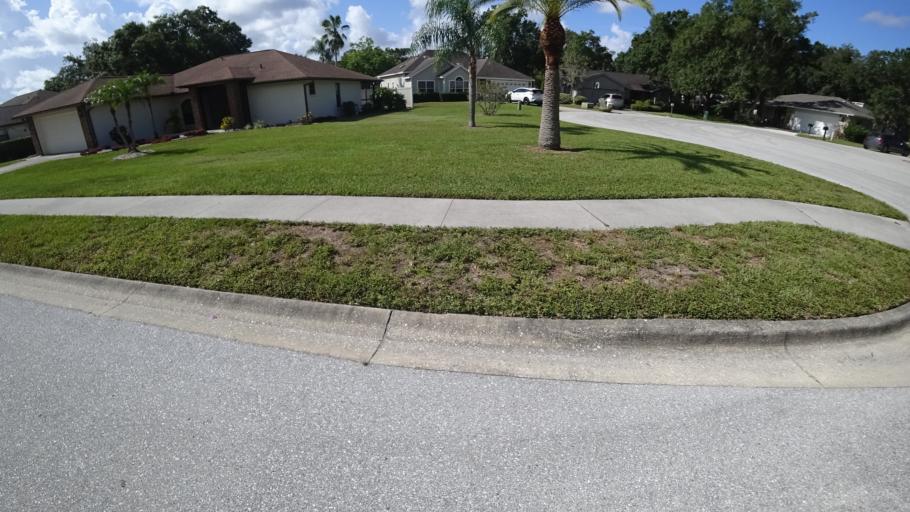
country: US
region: Florida
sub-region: Sarasota County
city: Desoto Lakes
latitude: 27.3994
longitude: -82.4990
